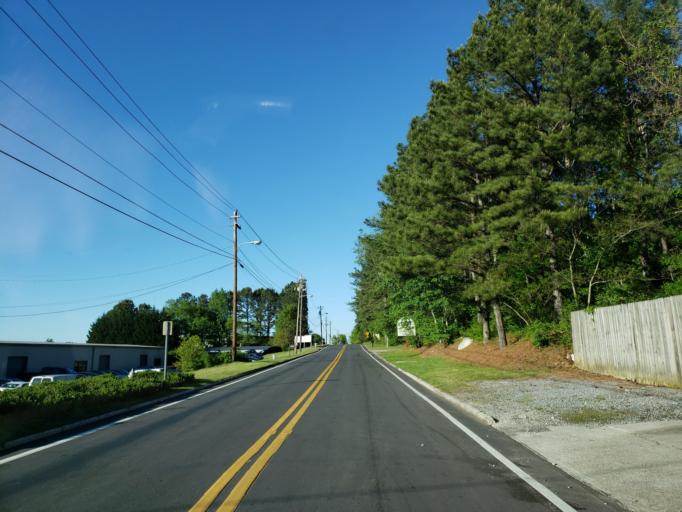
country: US
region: Georgia
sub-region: Cobb County
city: Smyrna
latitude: 33.9027
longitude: -84.4987
